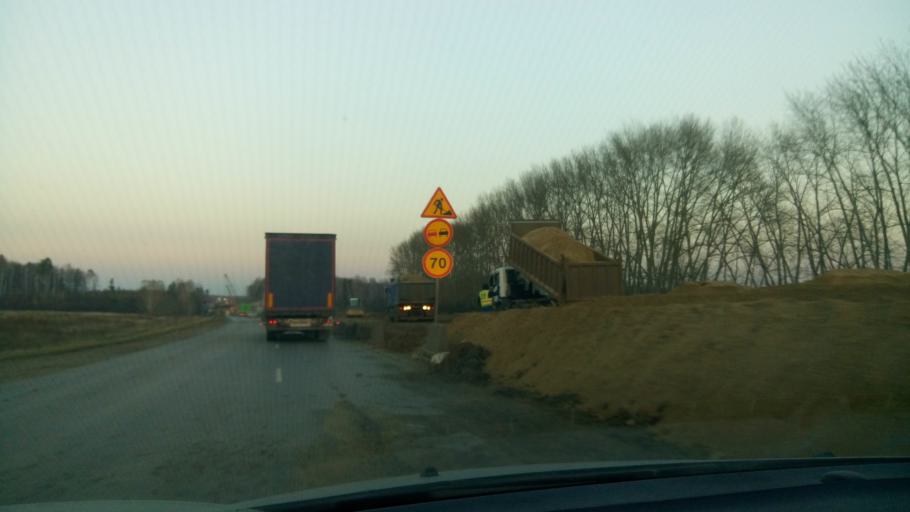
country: RU
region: Sverdlovsk
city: Pyshma
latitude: 56.9069
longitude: 63.1068
